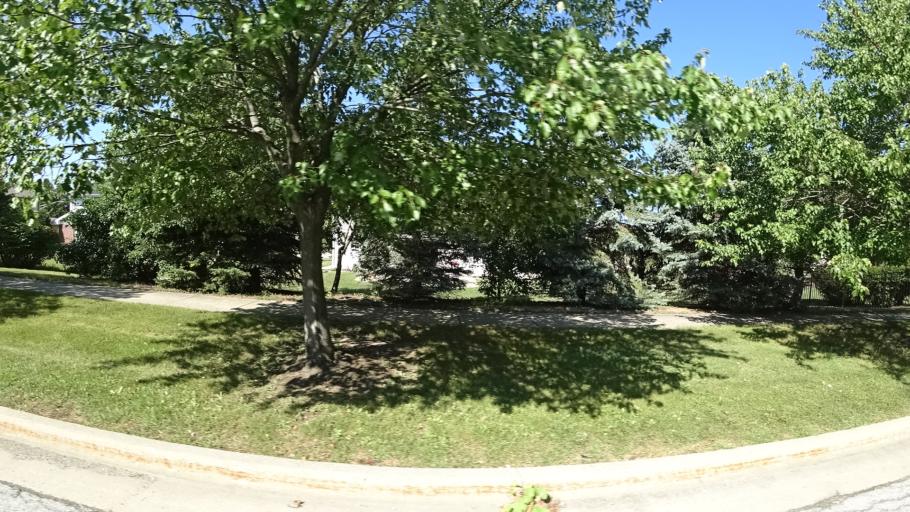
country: US
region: Illinois
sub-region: Cook County
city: Palos Park
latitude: 41.6371
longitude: -87.8151
